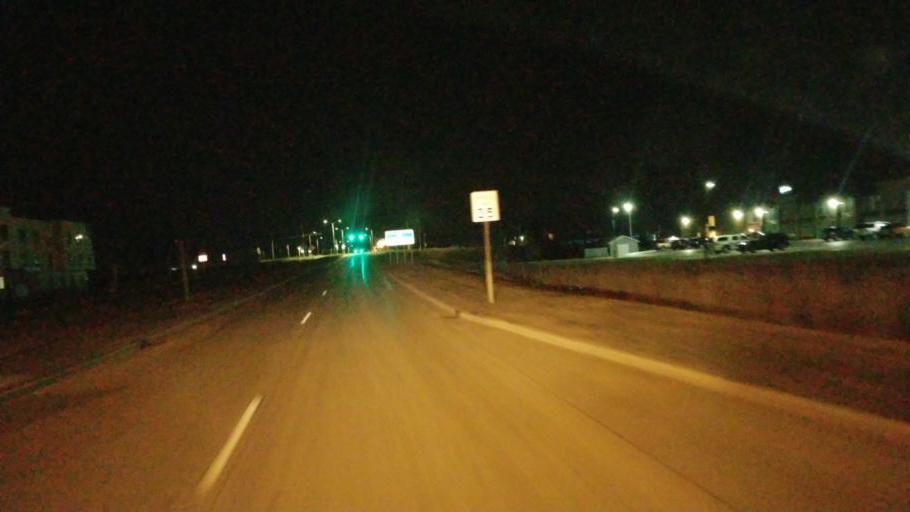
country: US
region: Wisconsin
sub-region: Fond du Lac County
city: Fond du Lac
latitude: 43.7565
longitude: -88.4780
